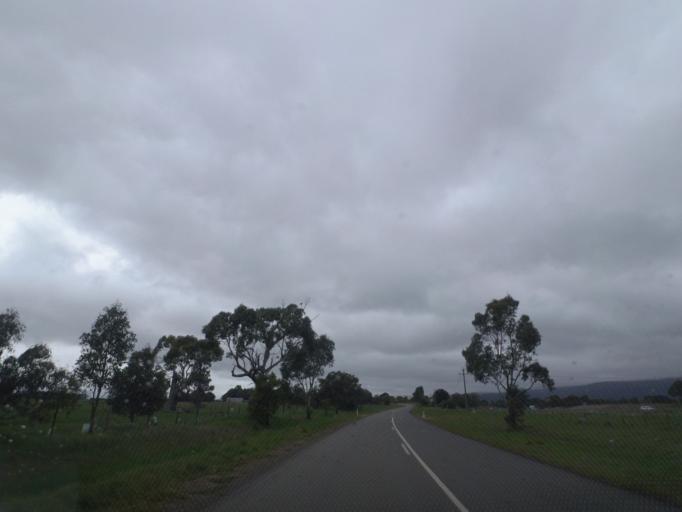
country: AU
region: Victoria
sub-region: Hume
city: Sunbury
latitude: -37.3222
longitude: 144.5429
